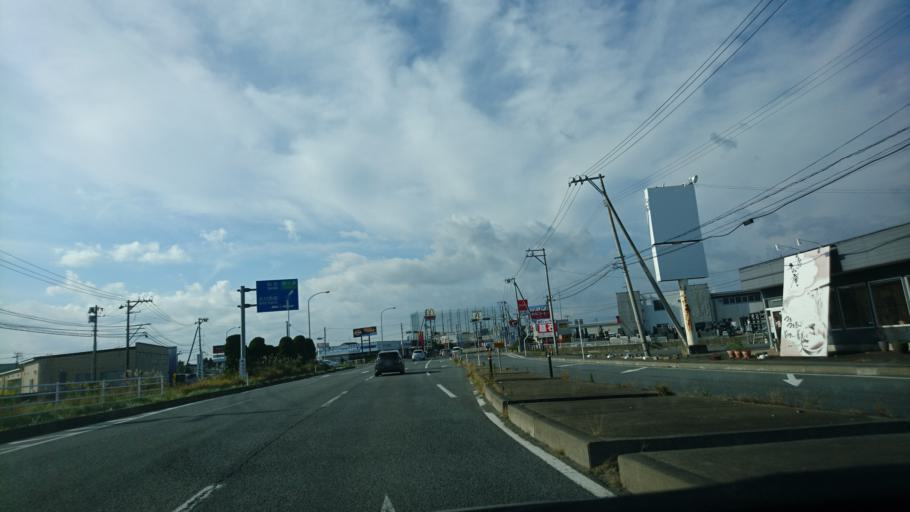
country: JP
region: Miyagi
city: Furukawa
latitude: 38.6047
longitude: 140.9805
